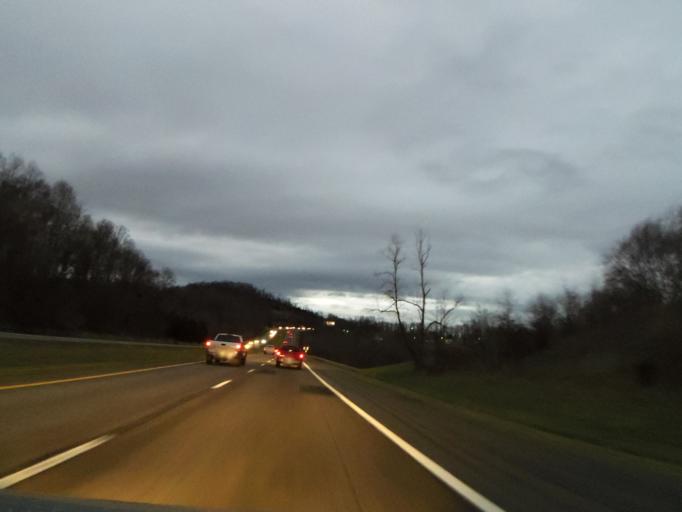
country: US
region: Tennessee
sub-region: Washington County
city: Oak Grove
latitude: 36.3850
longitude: -82.4316
